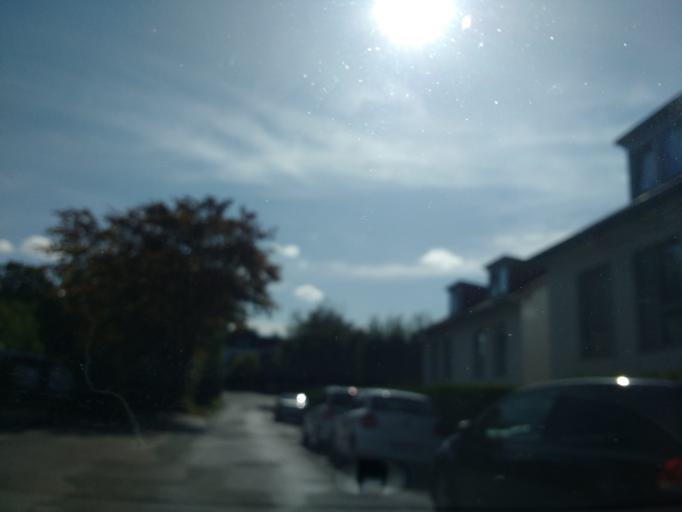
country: DE
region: North Rhine-Westphalia
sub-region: Regierungsbezirk Detmold
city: Detmold
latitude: 51.9406
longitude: 8.8945
